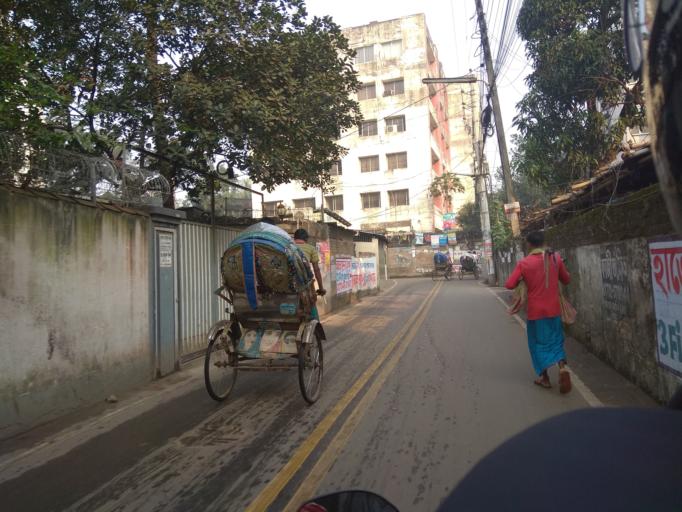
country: BD
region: Dhaka
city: Azimpur
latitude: 23.7574
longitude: 90.3819
